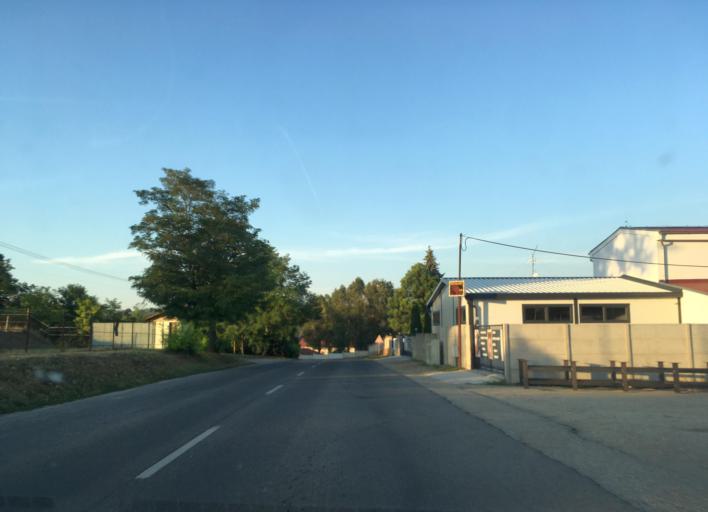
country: HU
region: Komarom-Esztergom
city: Neszmely
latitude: 47.8172
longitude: 18.3504
